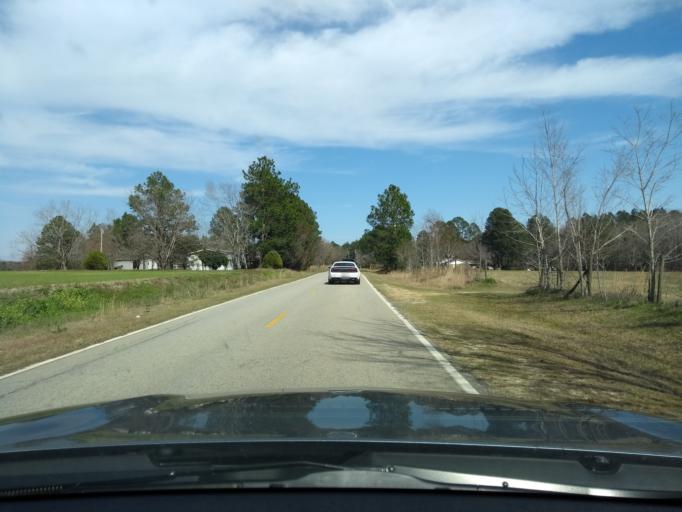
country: US
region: Georgia
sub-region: Bulloch County
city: Brooklet
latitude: 32.4698
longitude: -81.6411
